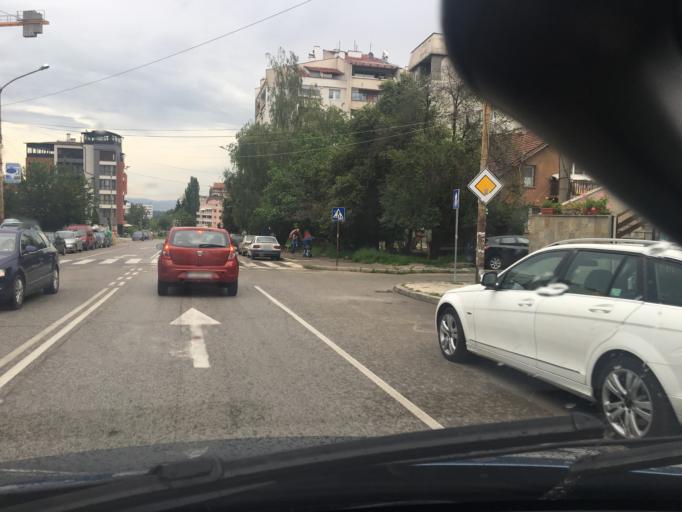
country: BG
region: Sofia-Capital
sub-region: Stolichna Obshtina
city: Sofia
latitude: 42.6622
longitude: 23.2655
